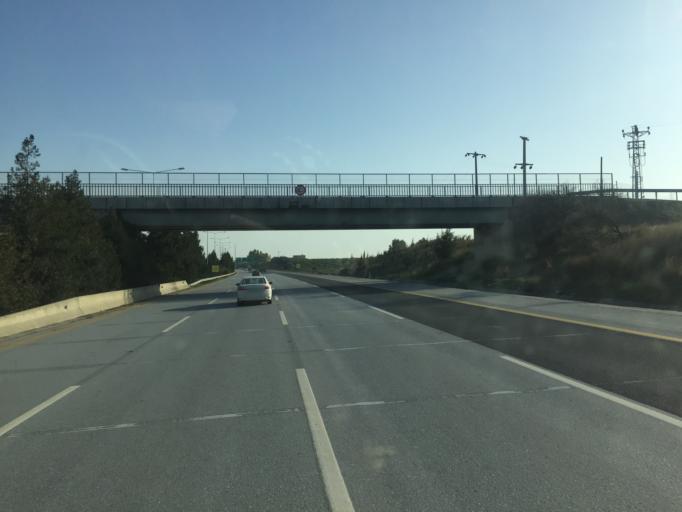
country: TR
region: Mersin
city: Yenice
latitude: 37.0252
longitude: 35.1048
